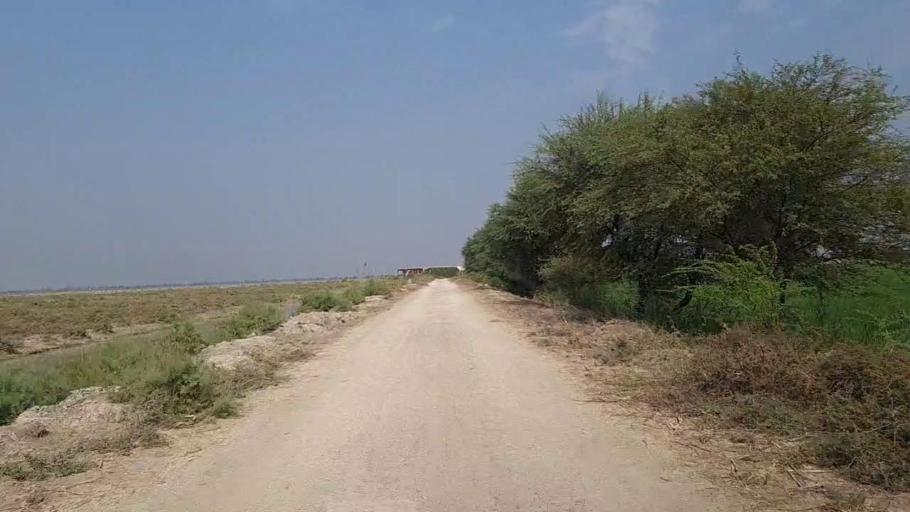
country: PK
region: Sindh
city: Mirwah Gorchani
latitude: 25.3763
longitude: 69.0424
